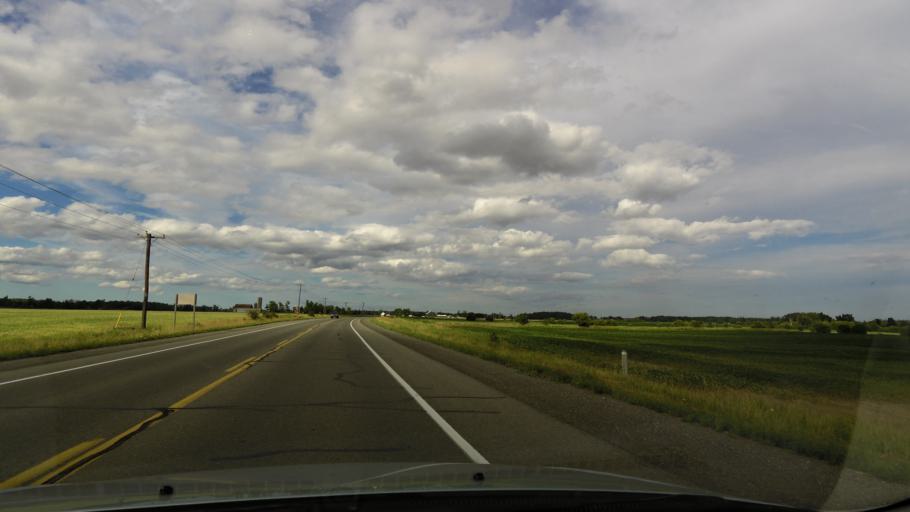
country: CA
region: Ontario
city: Brampton
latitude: 43.6776
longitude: -79.8859
